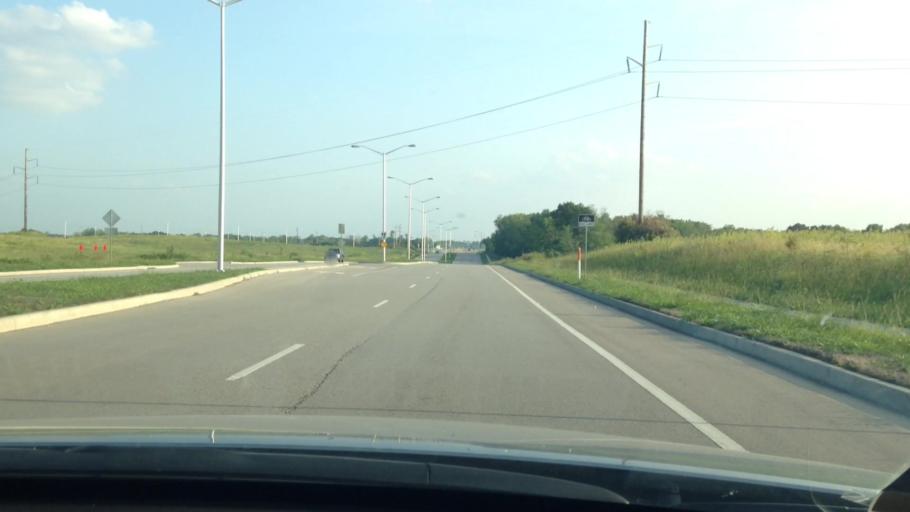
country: US
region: Missouri
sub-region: Platte County
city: Weatherby Lake
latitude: 39.2617
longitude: -94.6310
